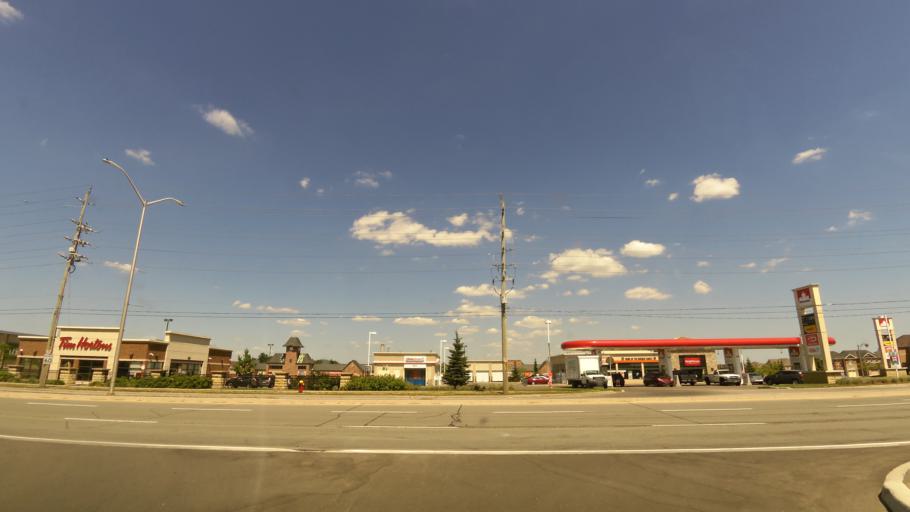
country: CA
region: Ontario
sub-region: Halton
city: Milton
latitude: 43.6302
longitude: -79.8769
